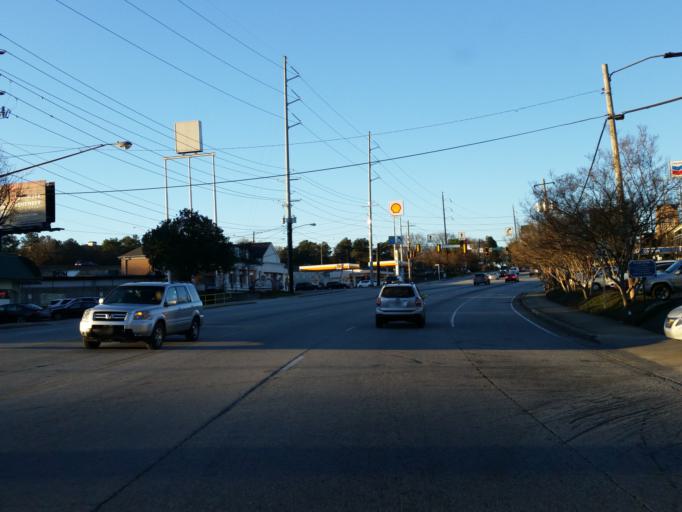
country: US
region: Georgia
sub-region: Cobb County
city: Vinings
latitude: 33.8479
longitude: -84.4296
